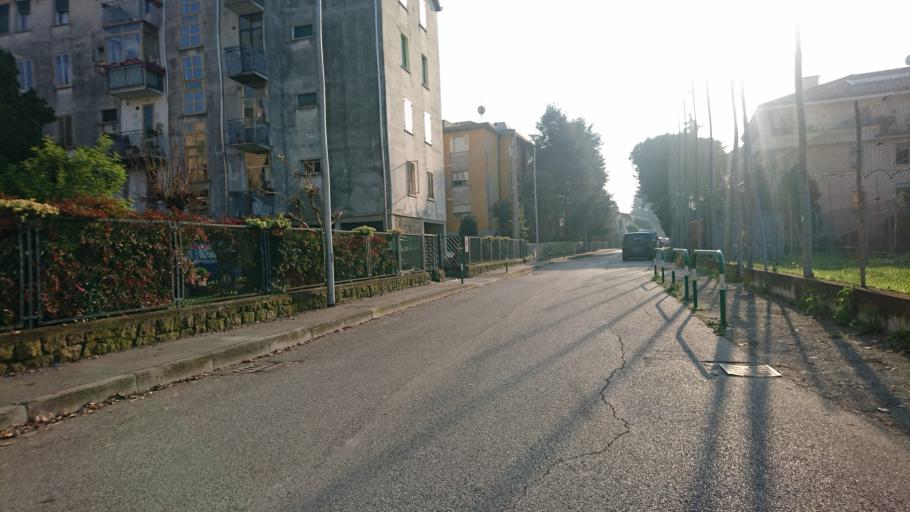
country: IT
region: Veneto
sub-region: Provincia di Padova
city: Caselle
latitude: 45.3980
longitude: 11.8276
